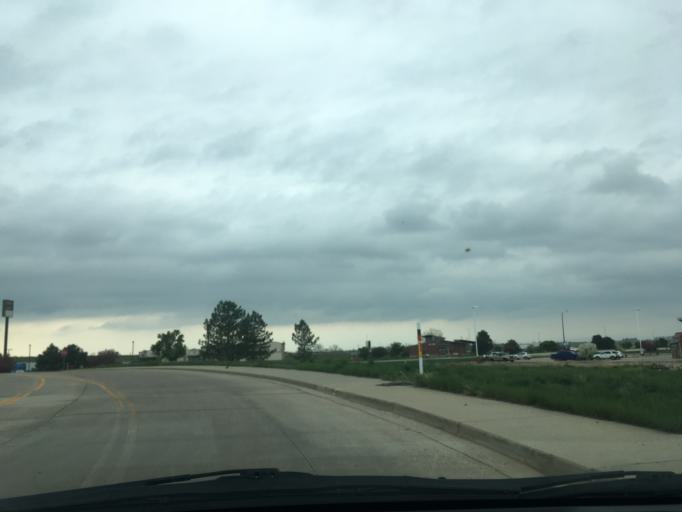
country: US
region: Colorado
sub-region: Weld County
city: Firestone
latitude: 40.1632
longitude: -104.9752
